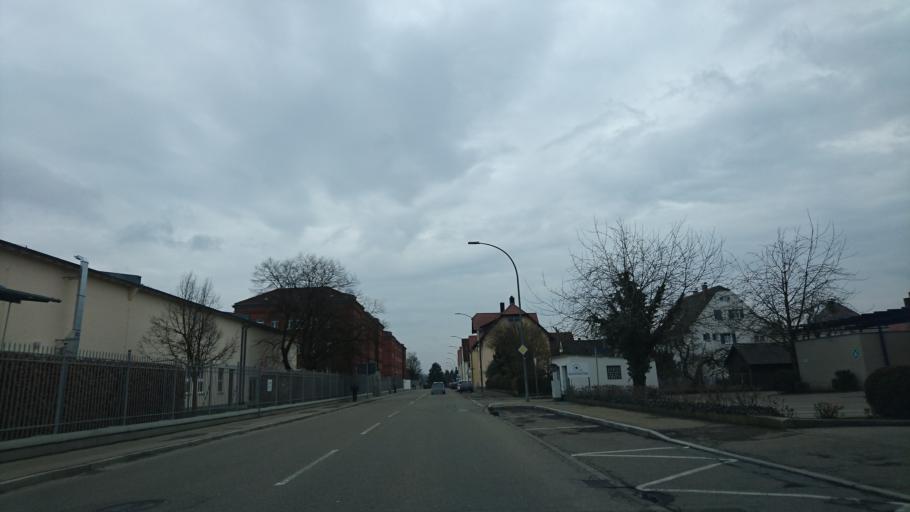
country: DE
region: Bavaria
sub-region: Swabia
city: Dillingen an der Donau
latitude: 48.5821
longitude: 10.5007
